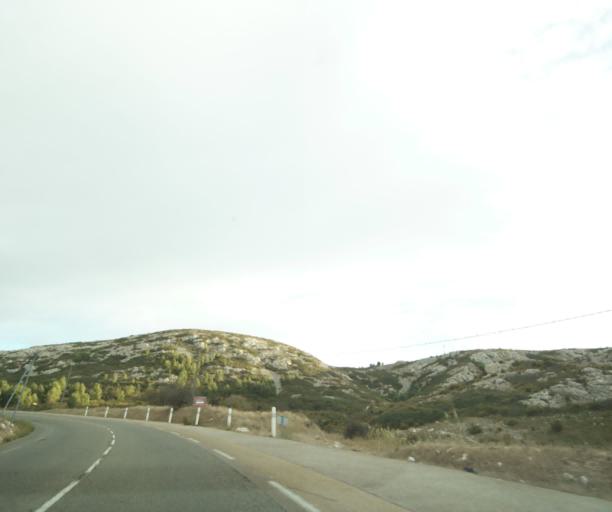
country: FR
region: Provence-Alpes-Cote d'Azur
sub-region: Departement des Bouches-du-Rhone
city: Le Rove
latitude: 43.3668
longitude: 5.2345
